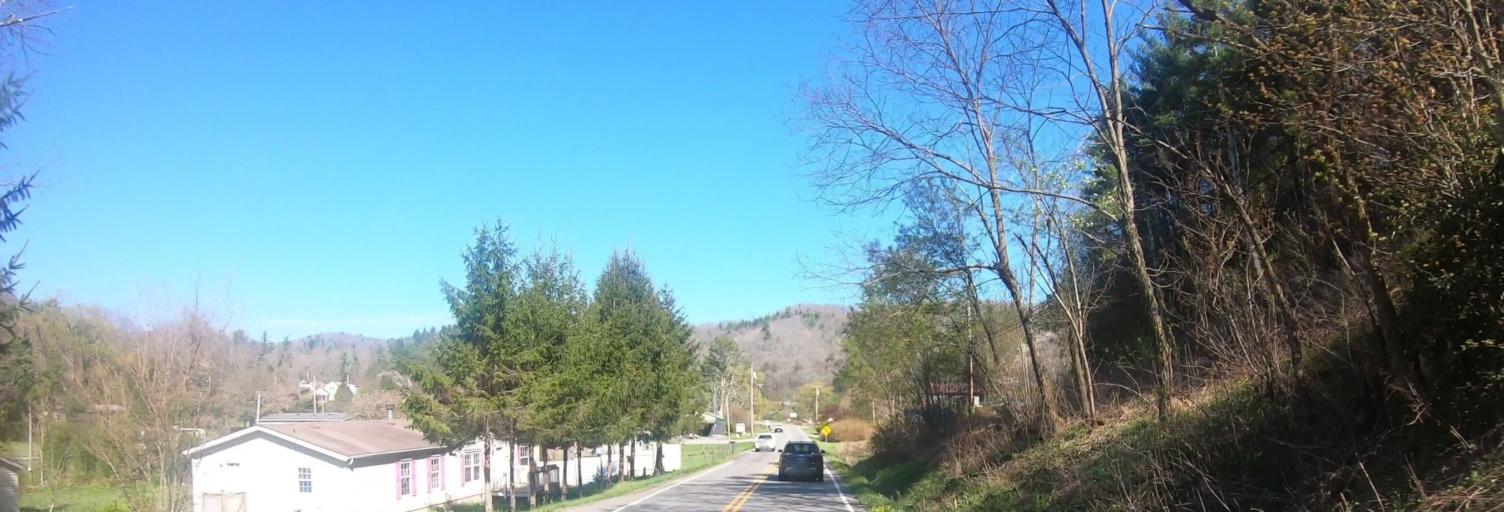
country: US
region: North Carolina
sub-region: Avery County
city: Newland
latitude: 36.0198
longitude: -81.9274
